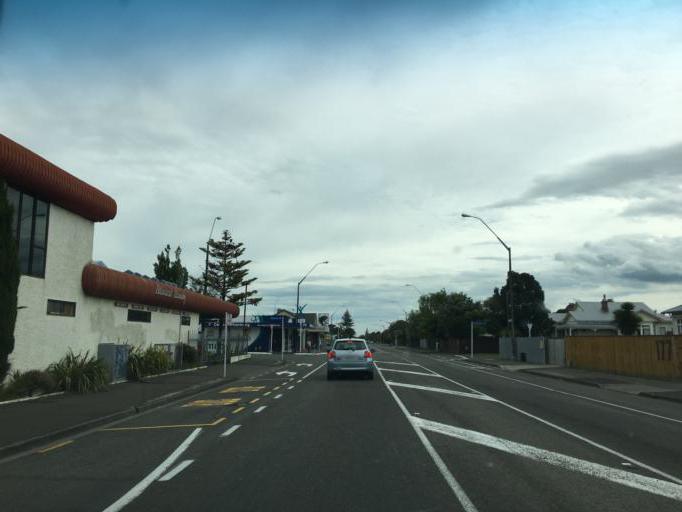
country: NZ
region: Manawatu-Wanganui
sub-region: Palmerston North City
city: Palmerston North
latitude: -40.3518
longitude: 175.6021
